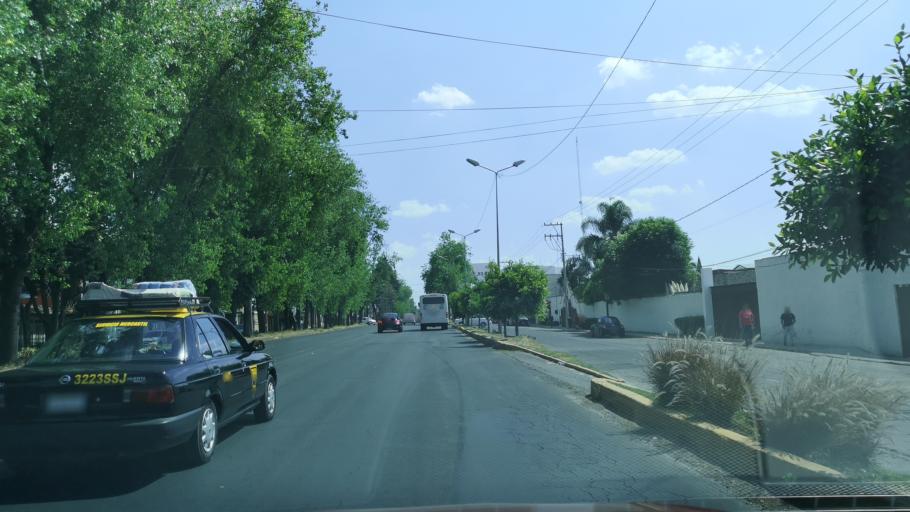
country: MX
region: Puebla
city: Puebla
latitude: 19.0727
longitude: -98.2188
